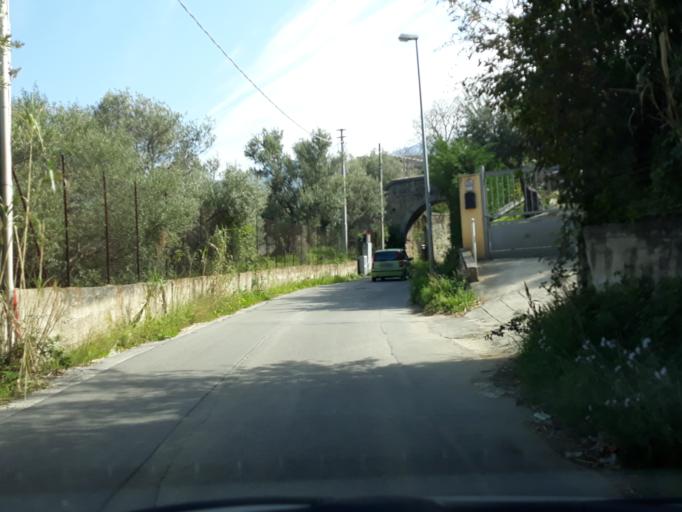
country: IT
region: Sicily
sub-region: Palermo
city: Monreale
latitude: 38.0721
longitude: 13.2832
